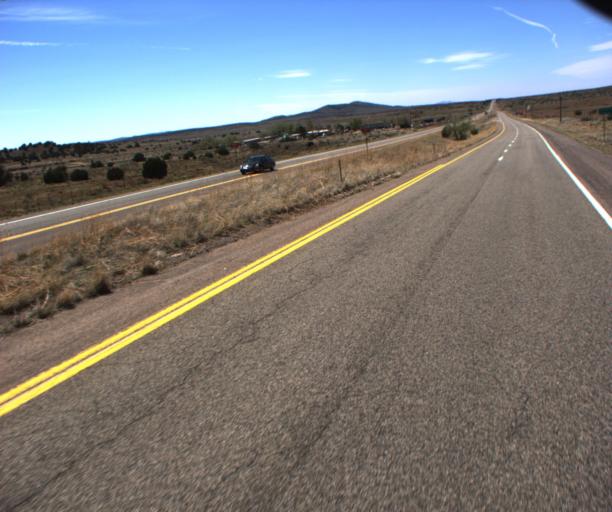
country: US
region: Arizona
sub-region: Mohave County
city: Peach Springs
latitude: 35.5286
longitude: -113.2253
